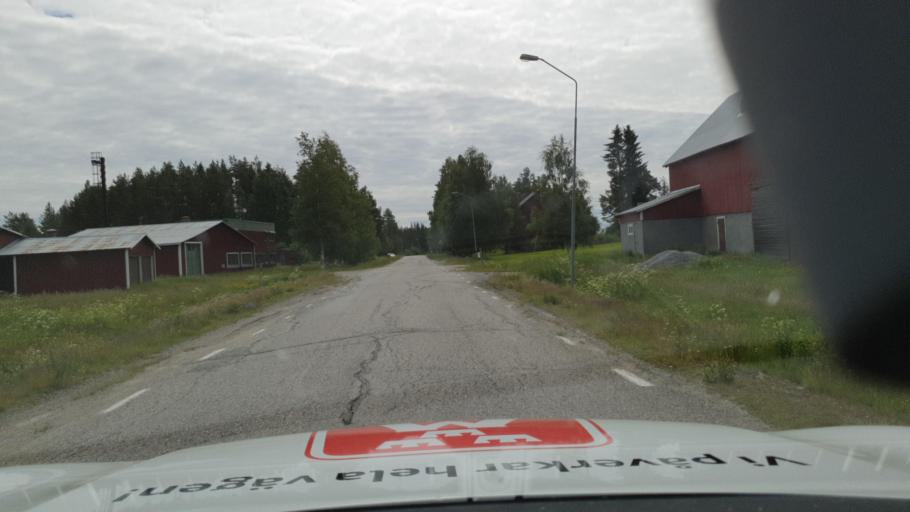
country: SE
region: Vaesterbotten
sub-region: Skelleftea Kommun
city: Forsbacka
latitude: 64.6191
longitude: 20.4992
